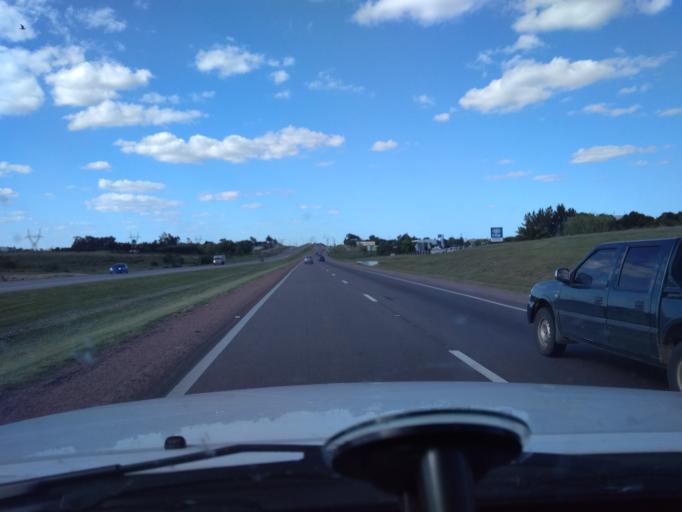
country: UY
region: Canelones
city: Las Piedras
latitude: -34.7304
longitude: -56.2486
